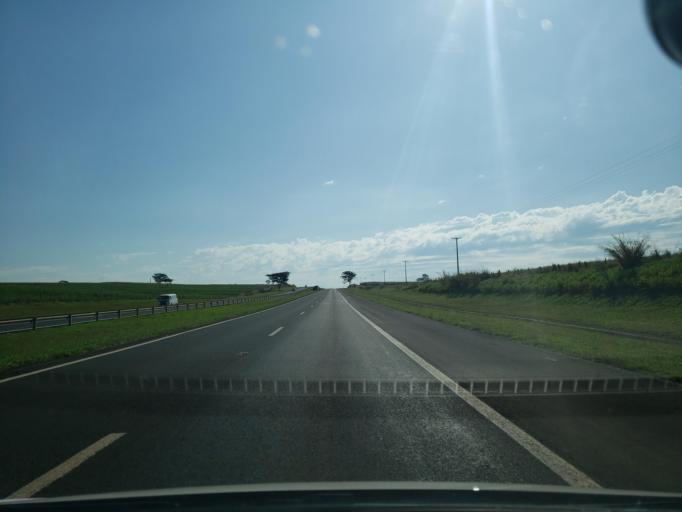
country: BR
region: Sao Paulo
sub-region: Promissao
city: Promissao
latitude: -21.5274
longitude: -49.9899
